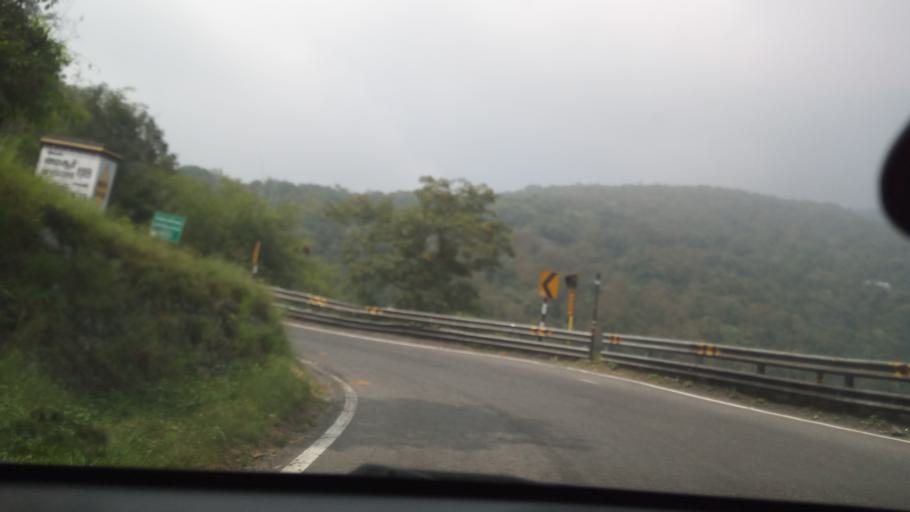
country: IN
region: Tamil Nadu
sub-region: Erode
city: Sathyamangalam
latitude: 11.6061
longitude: 77.1313
